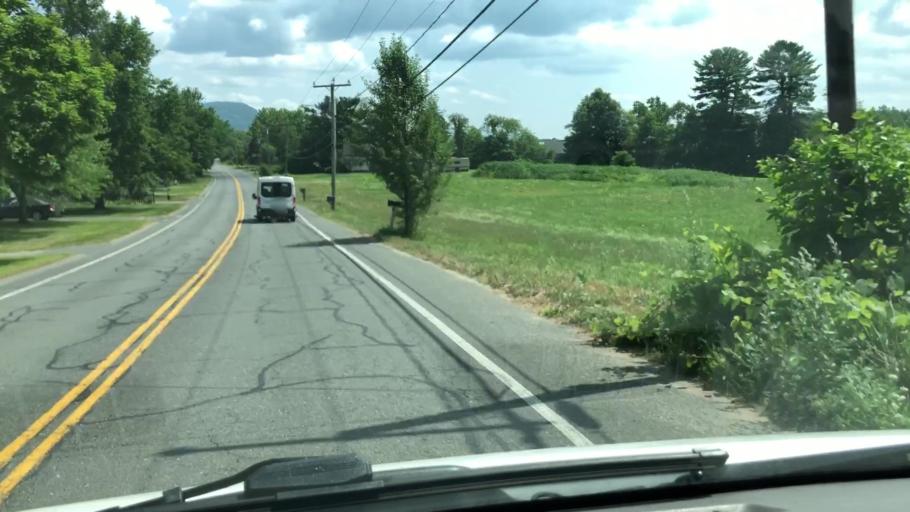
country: US
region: Massachusetts
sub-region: Hampshire County
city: Easthampton
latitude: 42.2866
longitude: -72.6721
